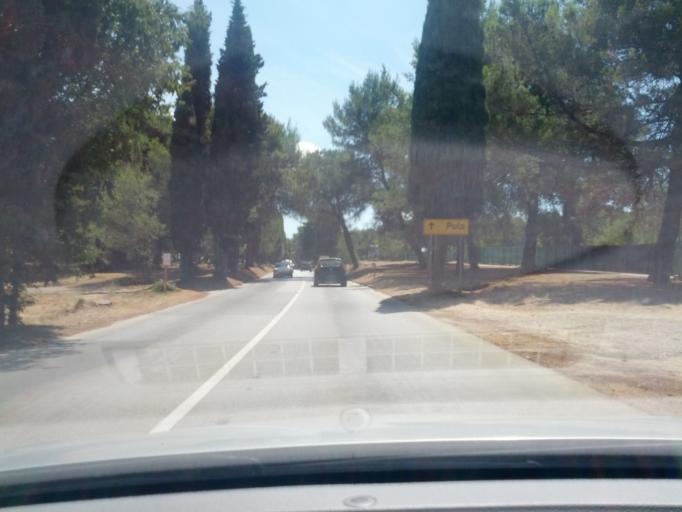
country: HR
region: Istarska
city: Fazana
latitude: 44.9198
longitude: 13.8089
